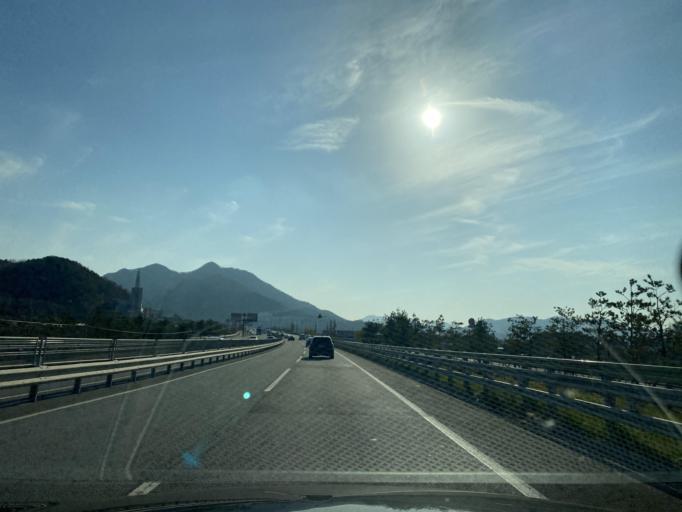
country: KR
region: Chungcheongnam-do
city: Asan
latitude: 36.7690
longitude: 127.0391
